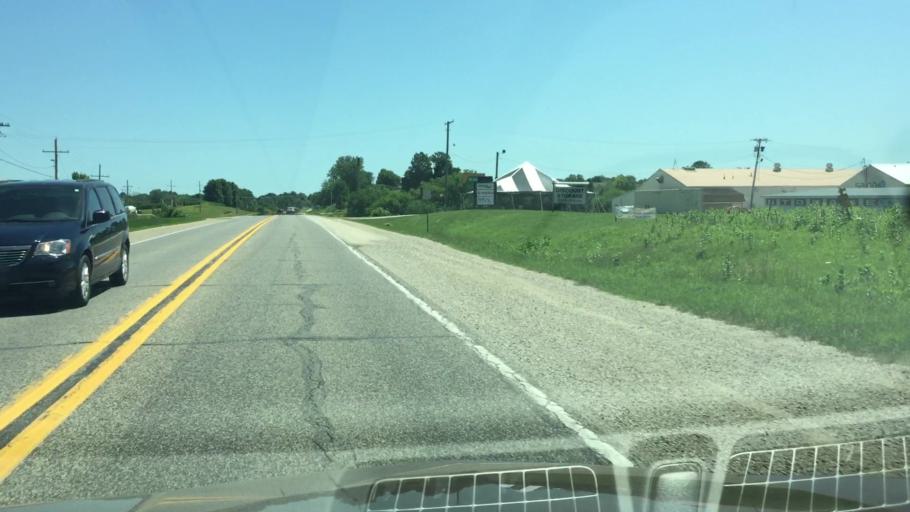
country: US
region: Iowa
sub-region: Linn County
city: Mount Vernon
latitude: 41.9170
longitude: -91.4050
